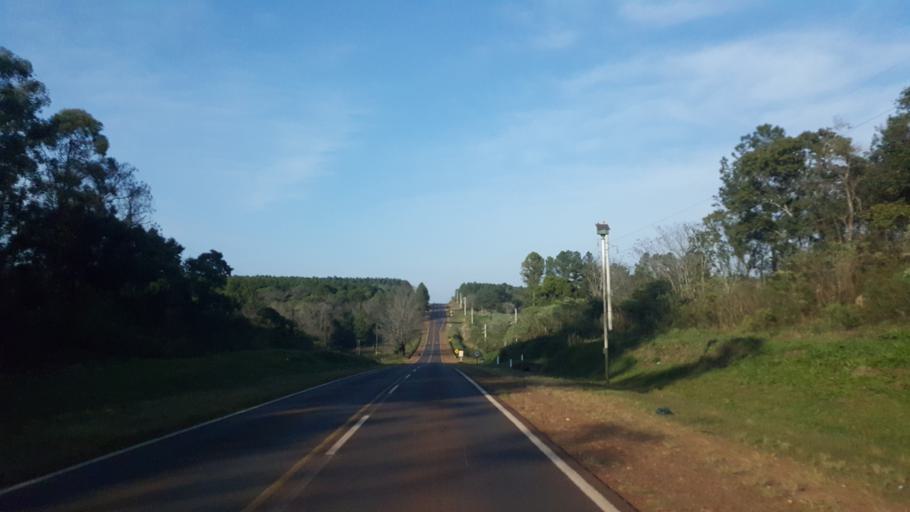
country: AR
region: Misiones
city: Capiovi
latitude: -26.8939
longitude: -55.0570
